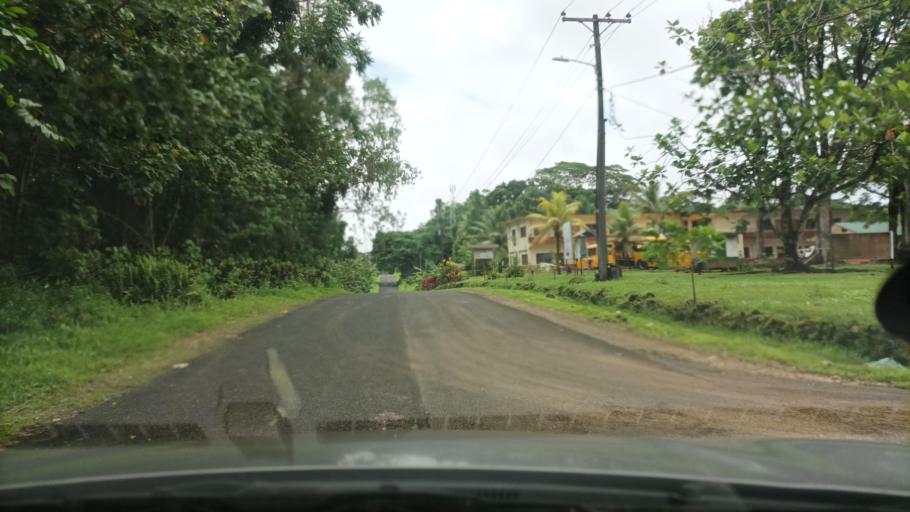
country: FM
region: Pohnpei
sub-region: Madolenihm Municipality
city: Madolenihm Municipality Government
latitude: 6.8348
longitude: 158.2982
